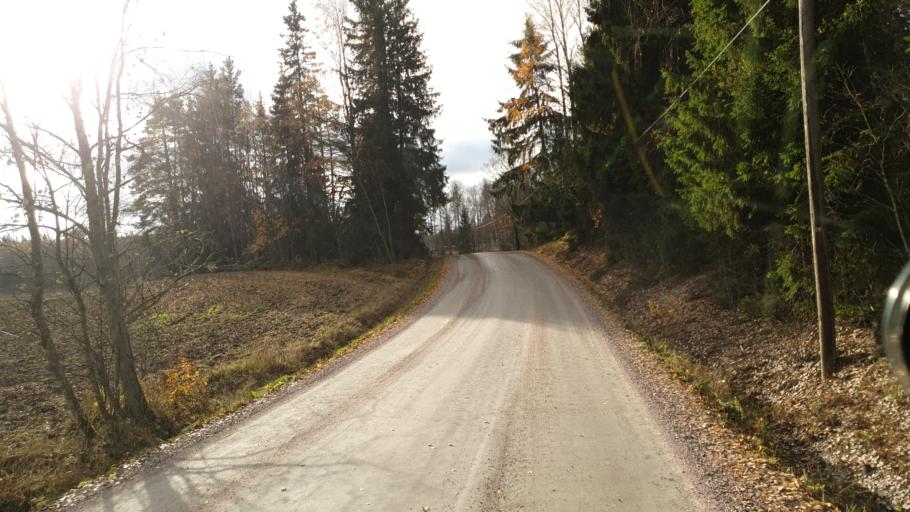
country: FI
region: Uusimaa
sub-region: Helsinki
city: Siuntio
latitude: 60.2386
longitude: 24.3048
